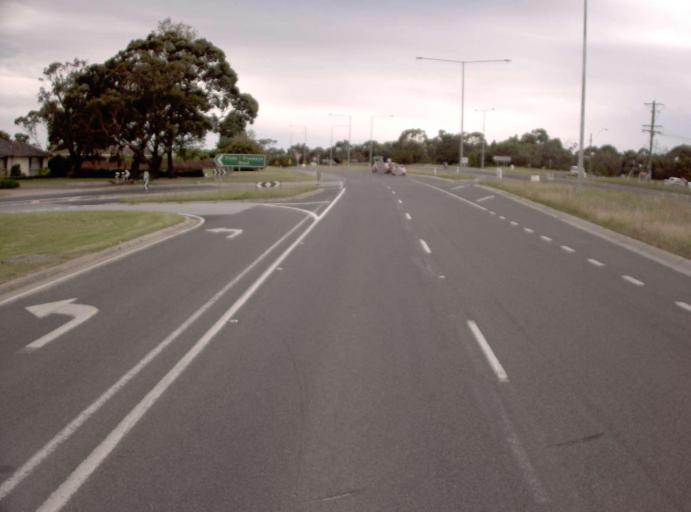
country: AU
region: Victoria
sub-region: Casey
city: Junction Village
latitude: -38.1592
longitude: 145.3184
